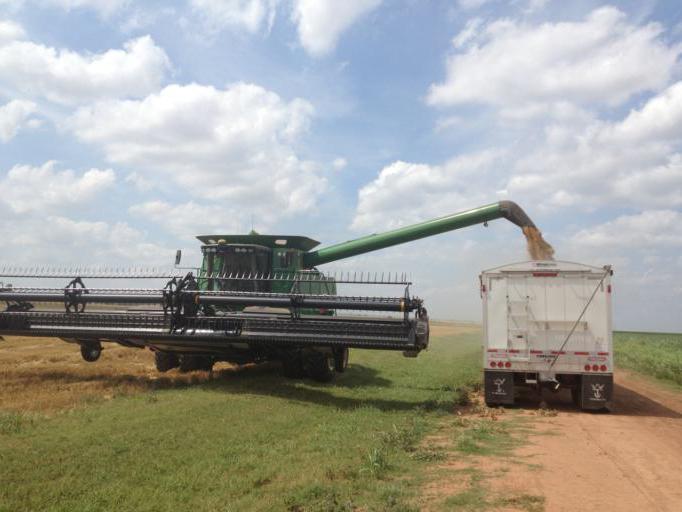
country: US
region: Oklahoma
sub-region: Alfalfa County
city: Helena
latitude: 36.6443
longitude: -98.0375
